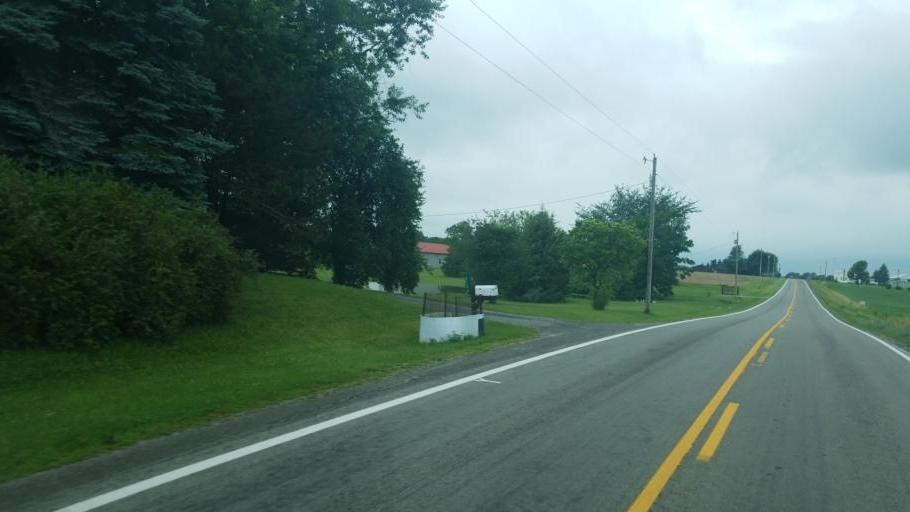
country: US
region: Ohio
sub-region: Logan County
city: Northwood
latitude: 40.5902
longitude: -83.7821
